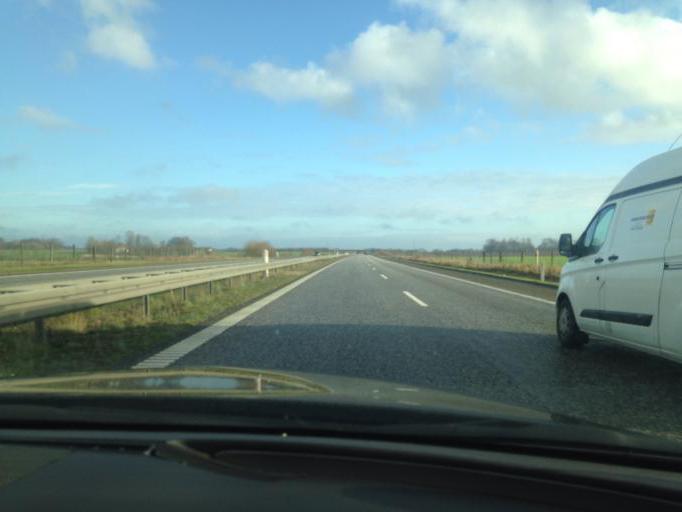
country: DK
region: South Denmark
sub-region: Kolding Kommune
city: Lunderskov
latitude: 55.5016
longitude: 9.2534
